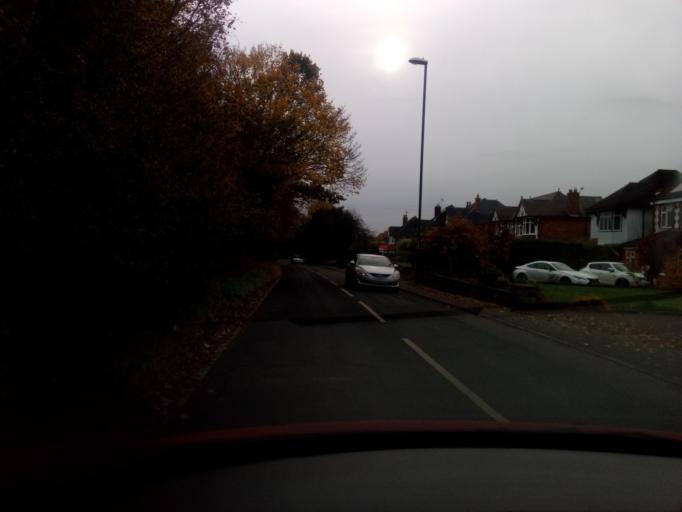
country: GB
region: England
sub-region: Derbyshire
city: Little Eaton
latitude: 52.9375
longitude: -1.4235
